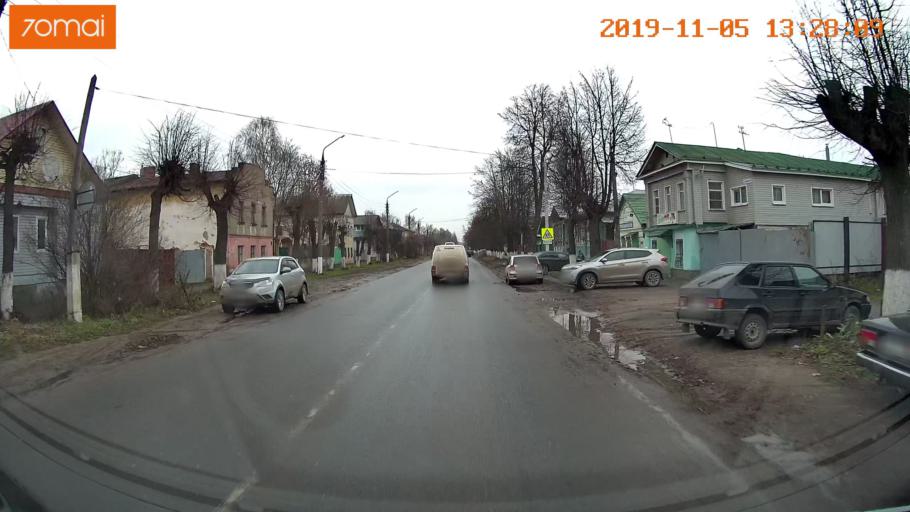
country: RU
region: Ivanovo
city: Shuya
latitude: 56.8558
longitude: 41.3855
